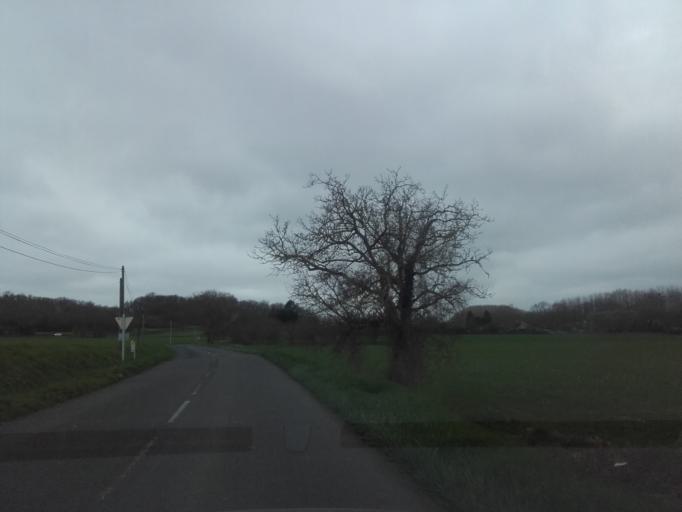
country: FR
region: Centre
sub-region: Departement d'Indre-et-Loire
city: Huismes
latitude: 47.2387
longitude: 0.2463
